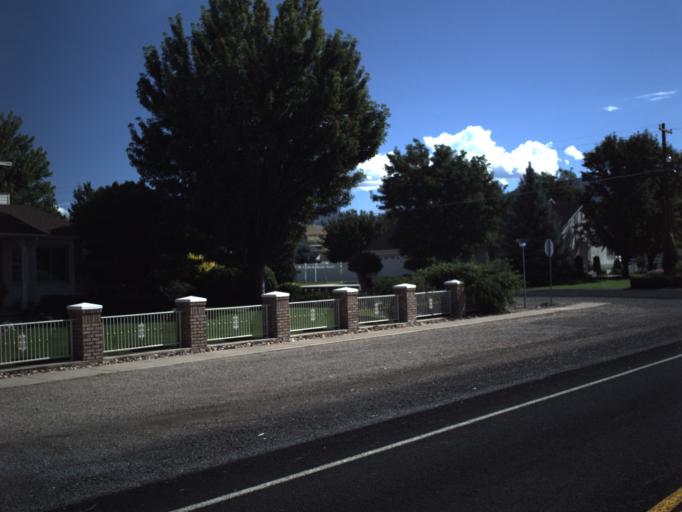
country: US
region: Utah
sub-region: Beaver County
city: Beaver
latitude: 38.2770
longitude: -112.6280
